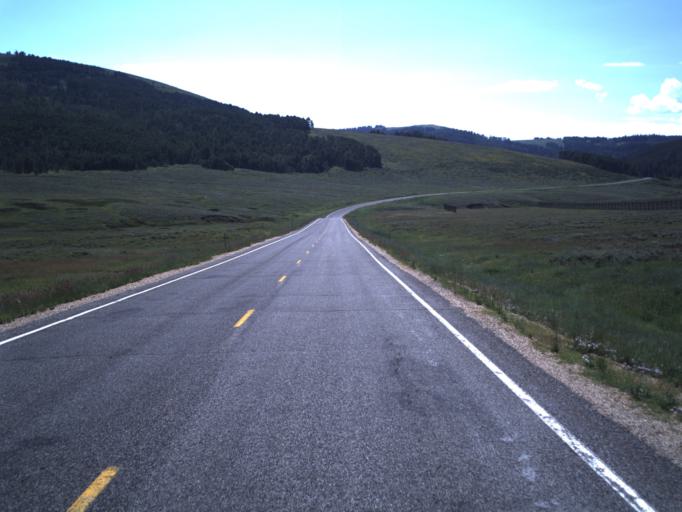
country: US
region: Utah
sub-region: Sanpete County
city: Fairview
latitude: 39.6698
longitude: -111.3073
